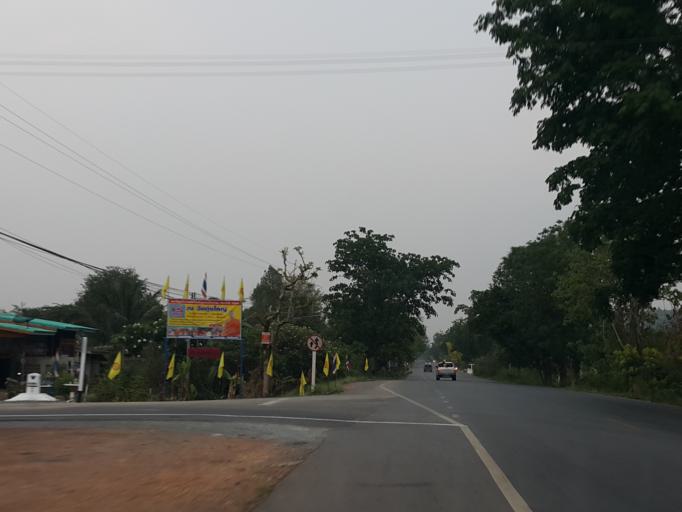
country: TH
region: Suphan Buri
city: Dan Chang
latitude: 14.9462
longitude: 99.6582
